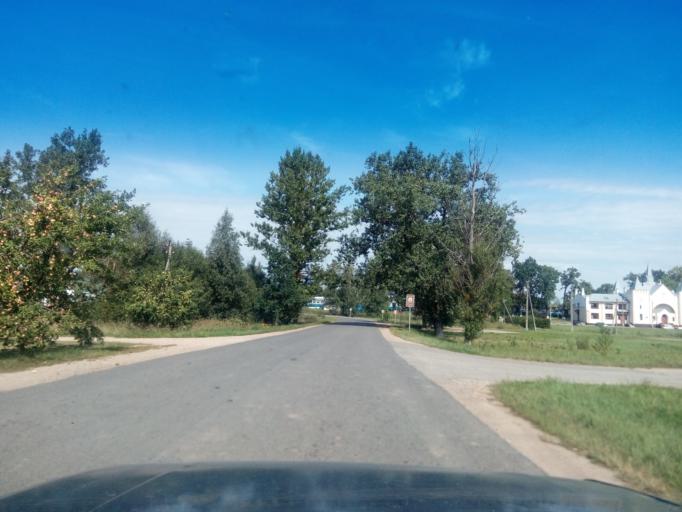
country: BY
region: Vitebsk
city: Vyerkhnyadzvinsk
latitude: 55.8328
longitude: 27.7350
